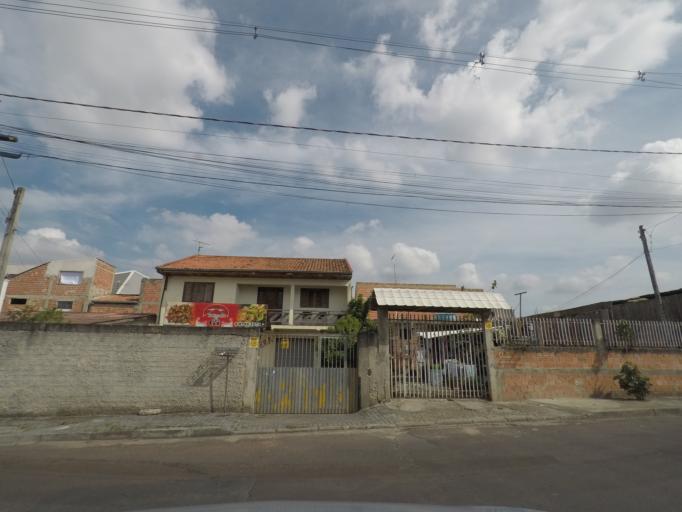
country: BR
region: Parana
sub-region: Sao Jose Dos Pinhais
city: Sao Jose dos Pinhais
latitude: -25.4883
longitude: -49.1974
